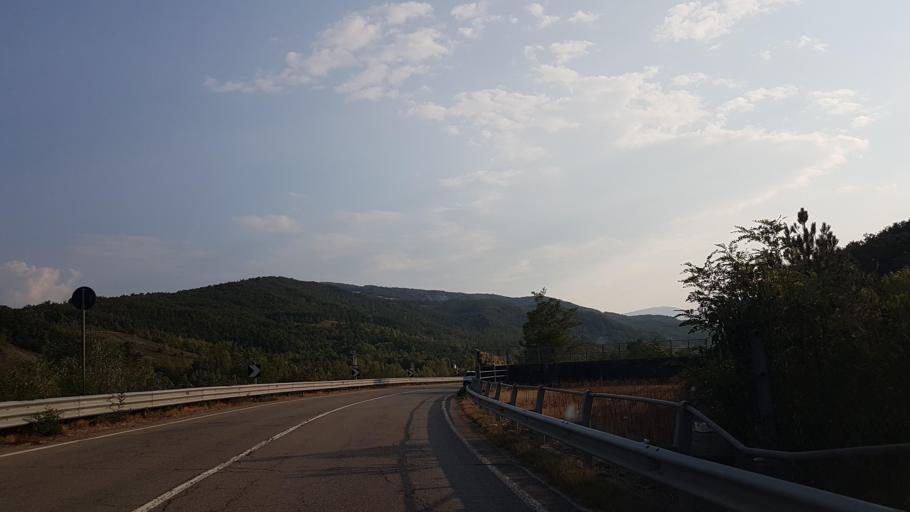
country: IT
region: Emilia-Romagna
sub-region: Provincia di Parma
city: Solignano
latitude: 44.6072
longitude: 9.9759
